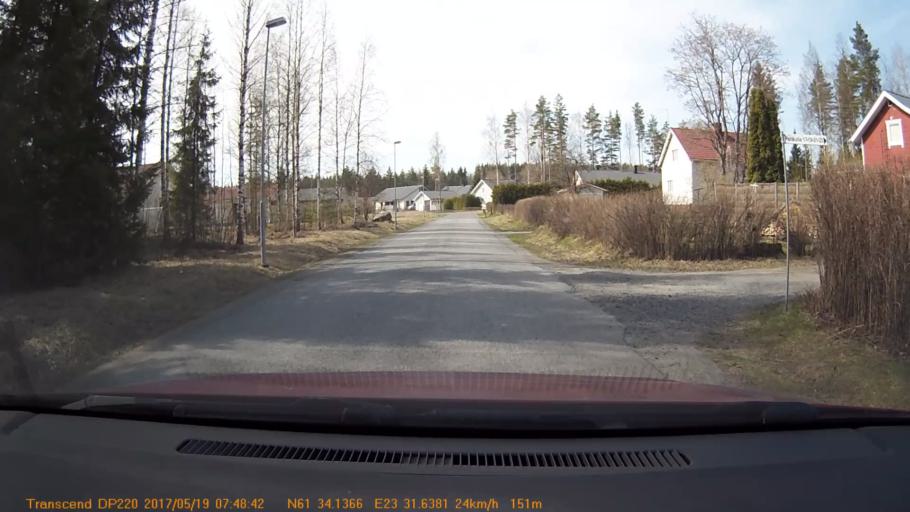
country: FI
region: Pirkanmaa
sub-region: Tampere
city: Yloejaervi
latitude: 61.5689
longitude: 23.5273
